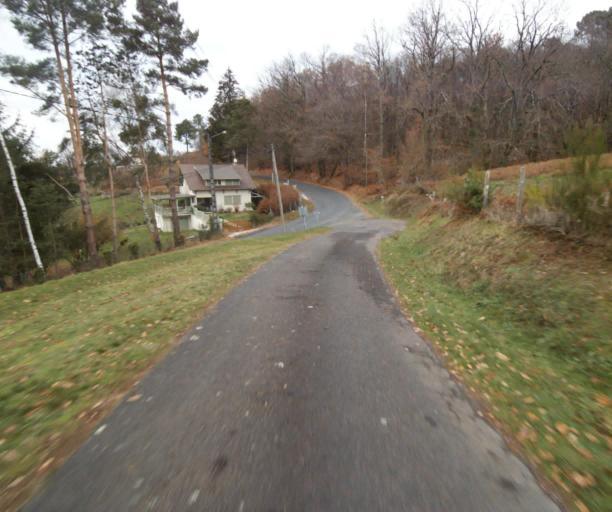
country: FR
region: Limousin
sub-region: Departement de la Correze
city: Cornil
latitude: 45.2294
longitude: 1.6562
